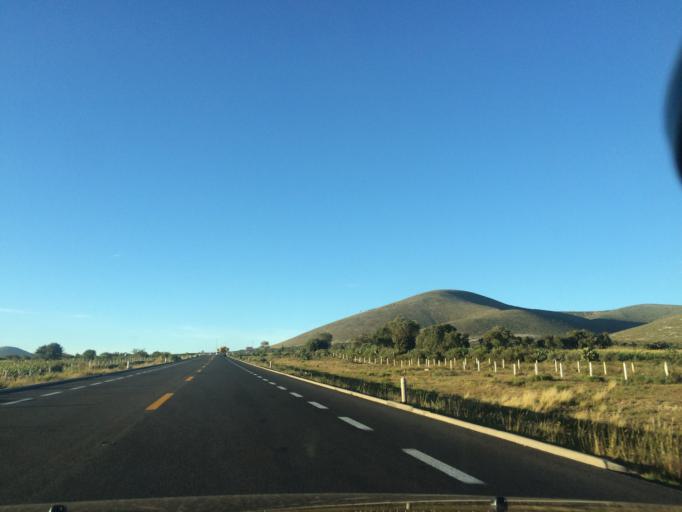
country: MX
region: Puebla
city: Morelos Canada
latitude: 18.7365
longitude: -97.4765
